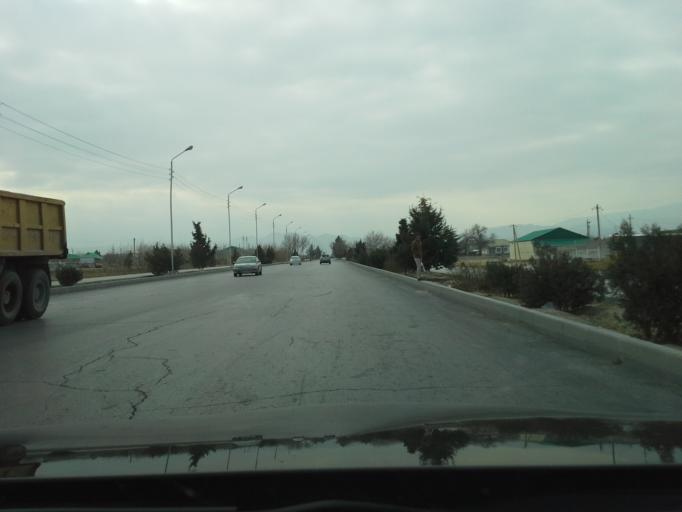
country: TM
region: Ahal
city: Abadan
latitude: 38.0337
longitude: 58.2687
